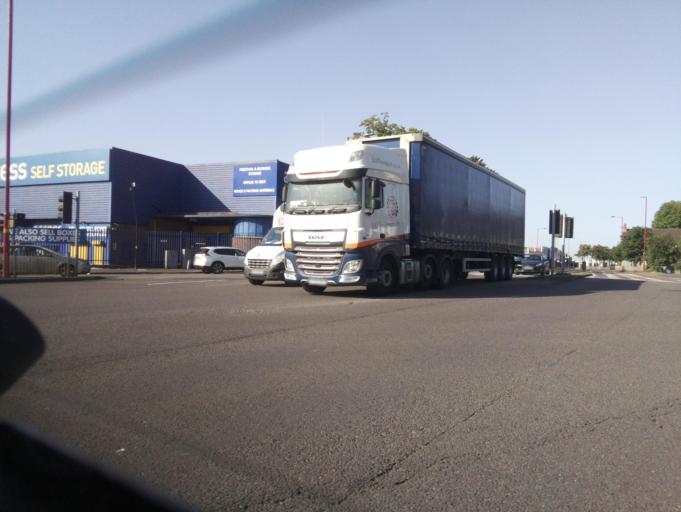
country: GB
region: England
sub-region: City and Borough of Birmingham
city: Sutton Coldfield
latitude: 52.5169
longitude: -1.8195
